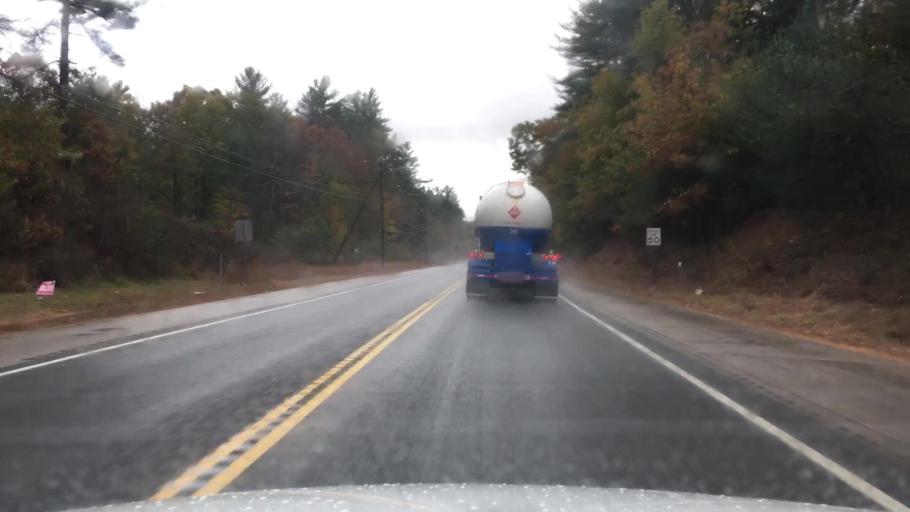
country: US
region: New Hampshire
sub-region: Strafford County
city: Barrington
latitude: 43.2055
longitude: -70.9969
